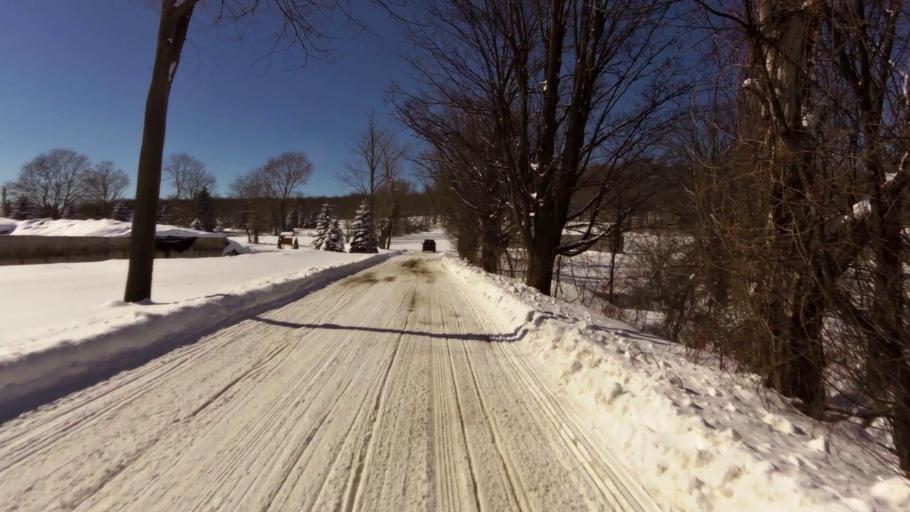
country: US
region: New York
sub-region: Chautauqua County
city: Mayville
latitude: 42.2464
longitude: -79.4415
